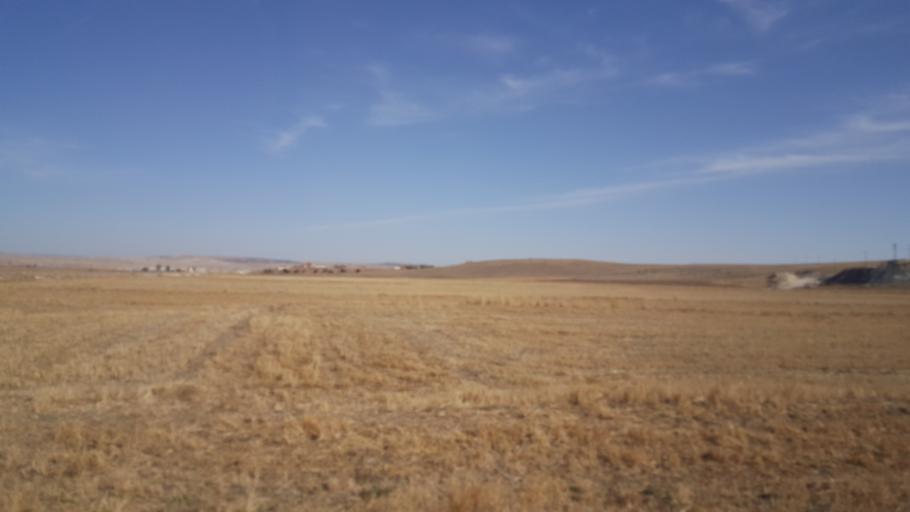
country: TR
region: Ankara
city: Yenice
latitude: 39.3822
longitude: 32.8224
